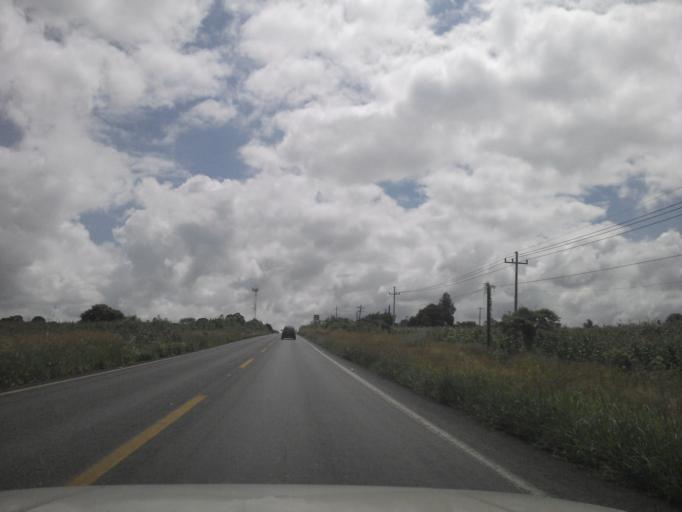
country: MX
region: Jalisco
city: Zapotlanejo
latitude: 20.6180
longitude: -103.0085
